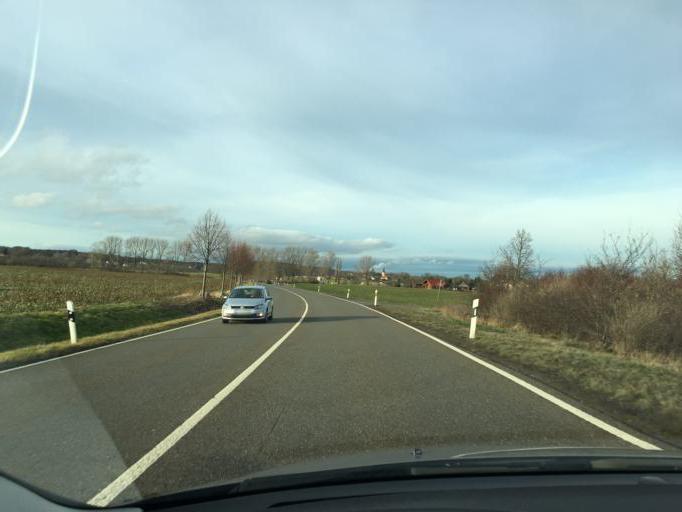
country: DE
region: Thuringia
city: Fockendorf
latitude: 51.0399
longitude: 12.4578
